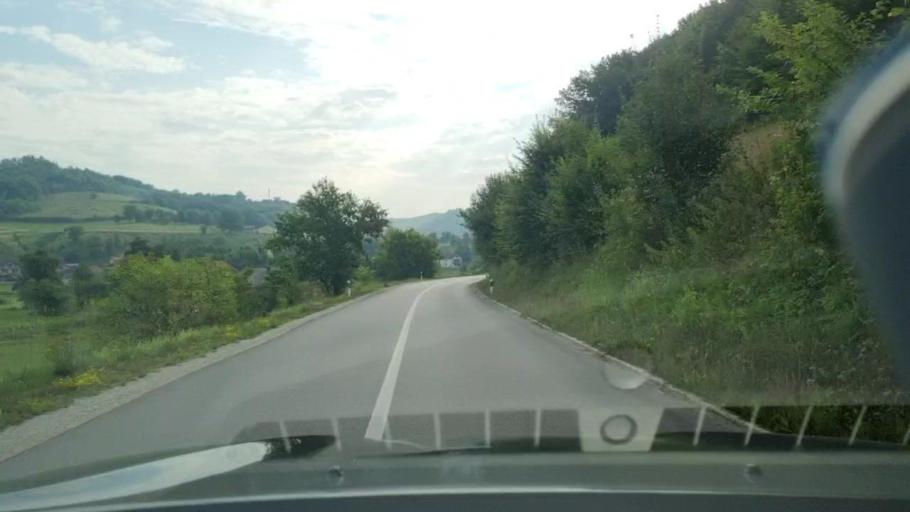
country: BA
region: Federation of Bosnia and Herzegovina
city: Vrnograc
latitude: 45.1599
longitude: 15.9411
